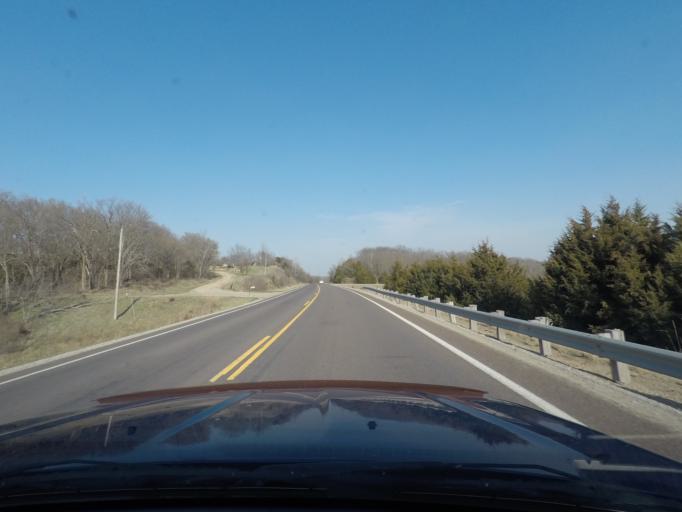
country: US
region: Kansas
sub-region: Douglas County
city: Lawrence
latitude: 39.0006
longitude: -95.3101
